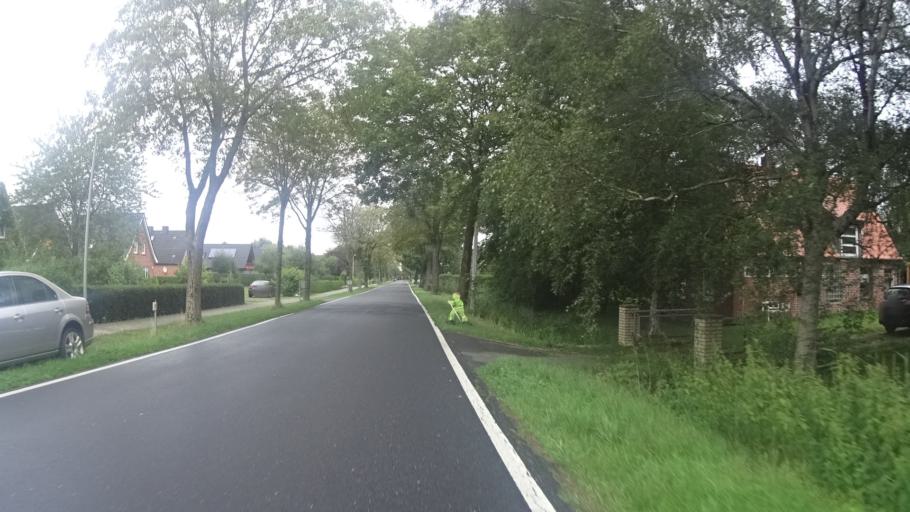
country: DE
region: Schleswig-Holstein
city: Altenmoor
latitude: 53.7814
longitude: 9.5578
